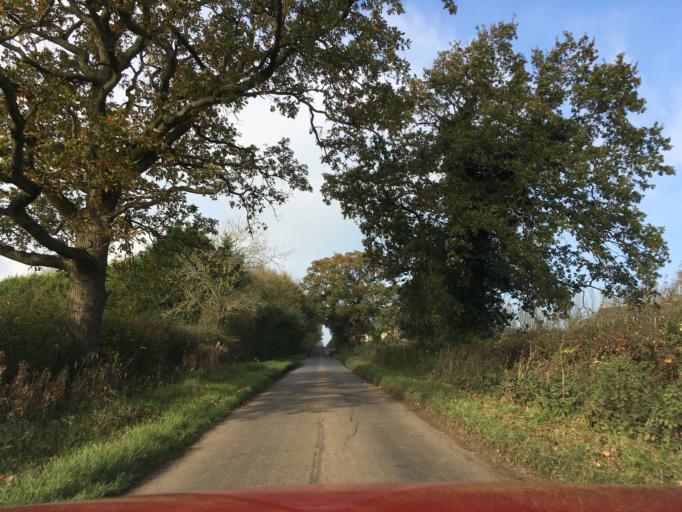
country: GB
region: England
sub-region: South Gloucestershire
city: Chipping Sodbury
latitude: 51.5667
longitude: -2.3863
